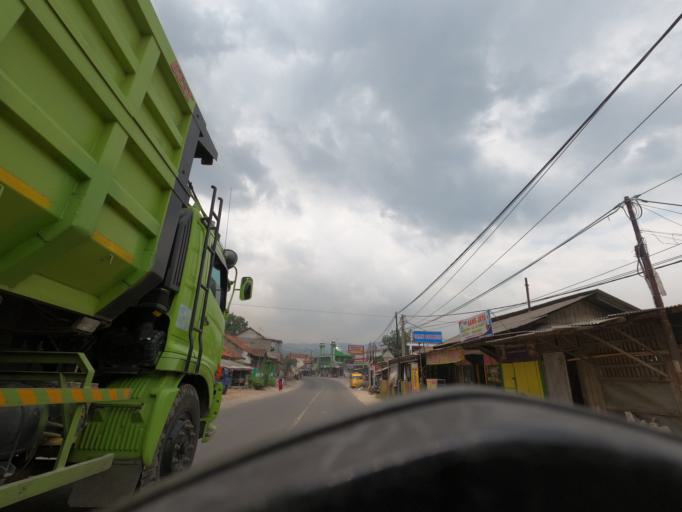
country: ID
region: West Java
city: Padalarang
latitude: -6.8318
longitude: 107.4289
